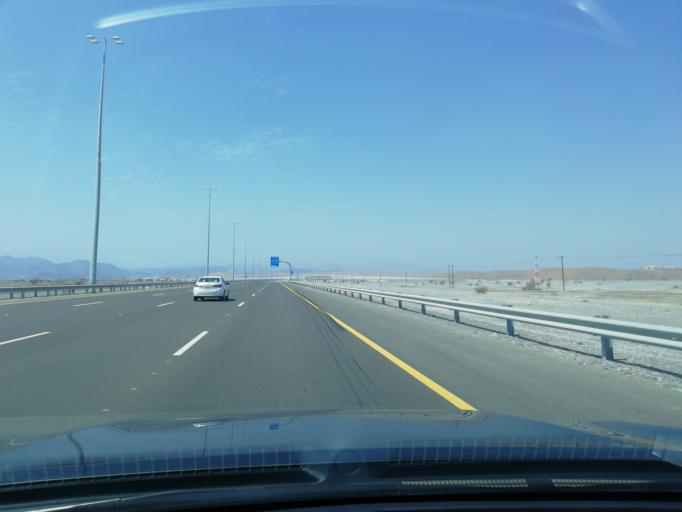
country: OM
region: Al Batinah
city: Barka'
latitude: 23.5360
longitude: 57.6729
